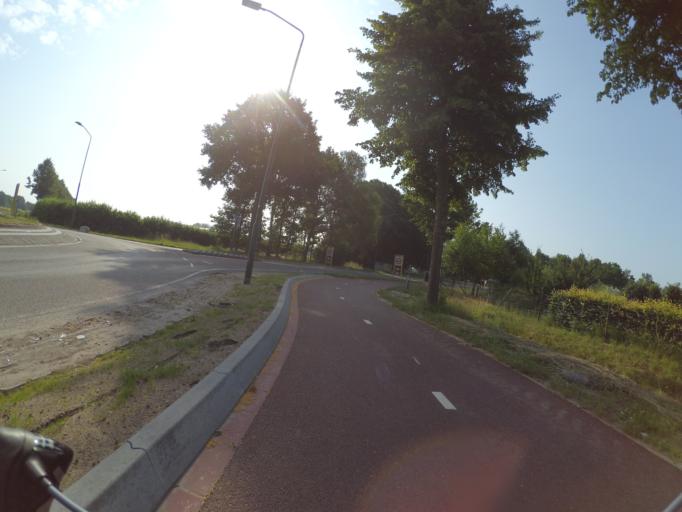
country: NL
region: North Brabant
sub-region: Gemeente Dongen
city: Dongen
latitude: 51.6379
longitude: 4.9572
